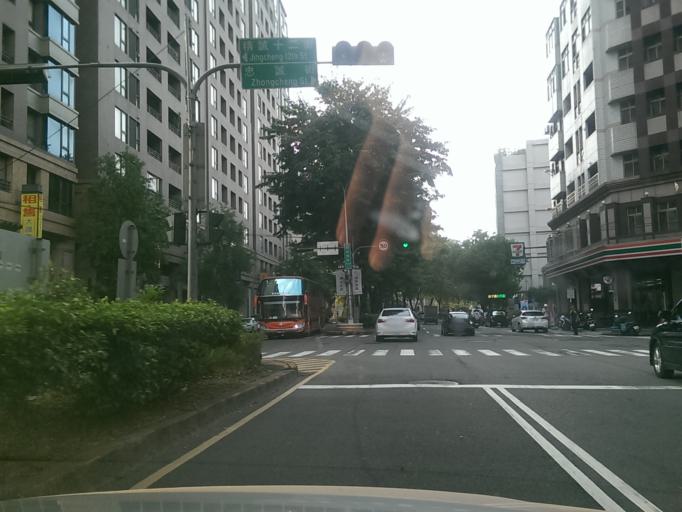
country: TW
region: Taiwan
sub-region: Taichung City
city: Taichung
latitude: 24.1524
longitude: 120.6573
